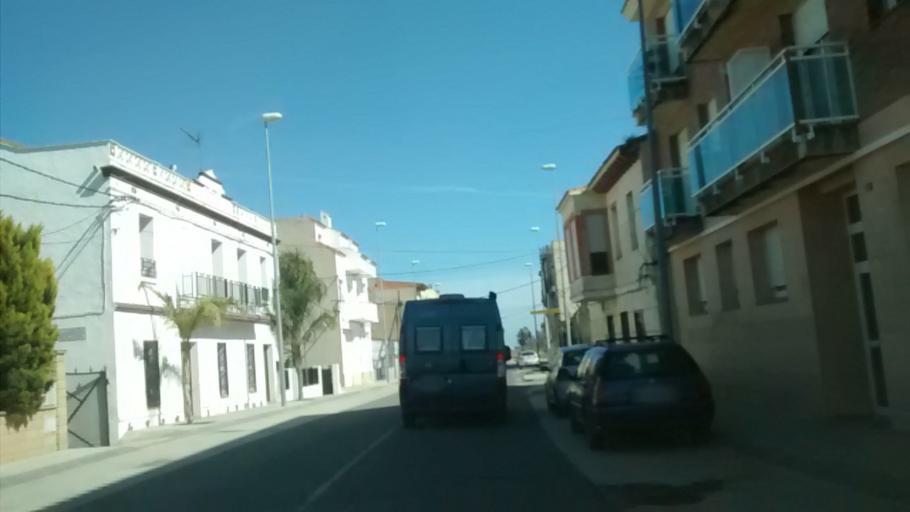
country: ES
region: Catalonia
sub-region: Provincia de Tarragona
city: Deltebre
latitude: 40.7149
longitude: 0.7481
